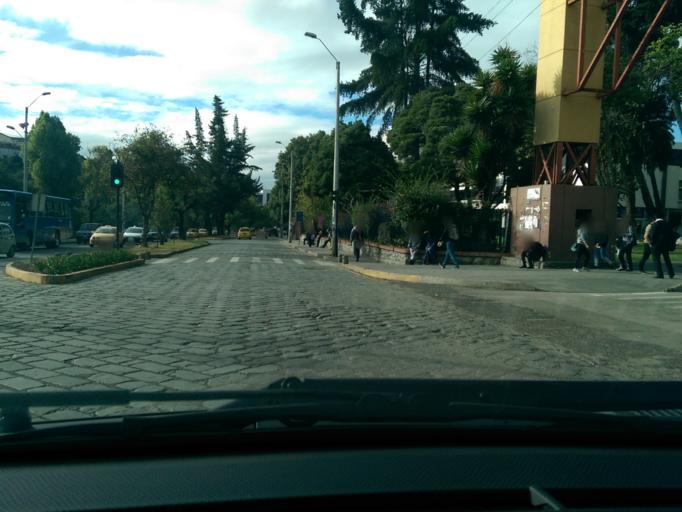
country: EC
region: Azuay
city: Cuenca
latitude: -2.8997
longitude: -79.0094
